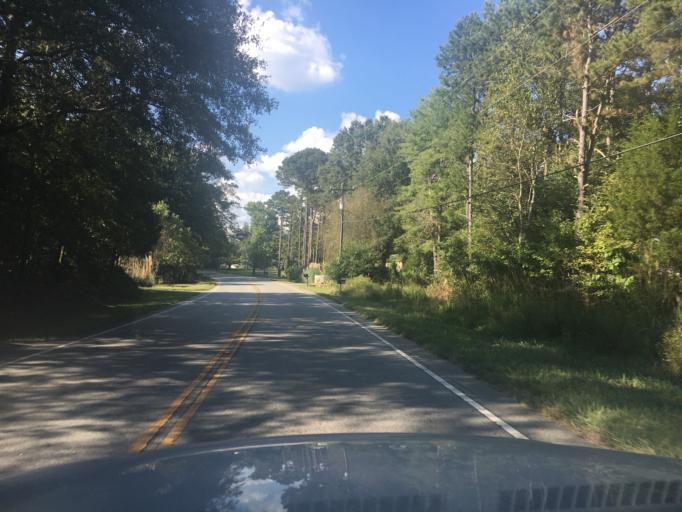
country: US
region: South Carolina
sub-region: Greenville County
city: Fountain Inn
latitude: 34.6559
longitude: -82.2577
